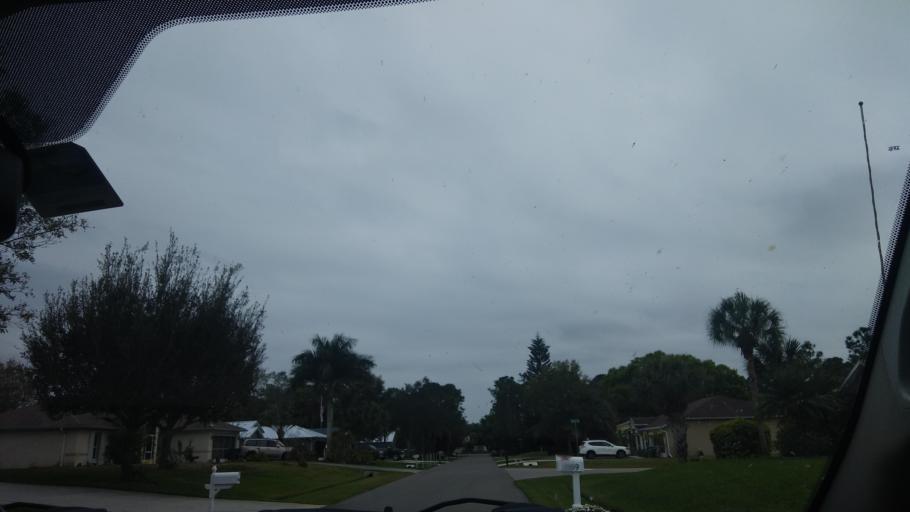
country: US
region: Florida
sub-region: Indian River County
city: Sebastian
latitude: 27.7591
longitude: -80.4913
